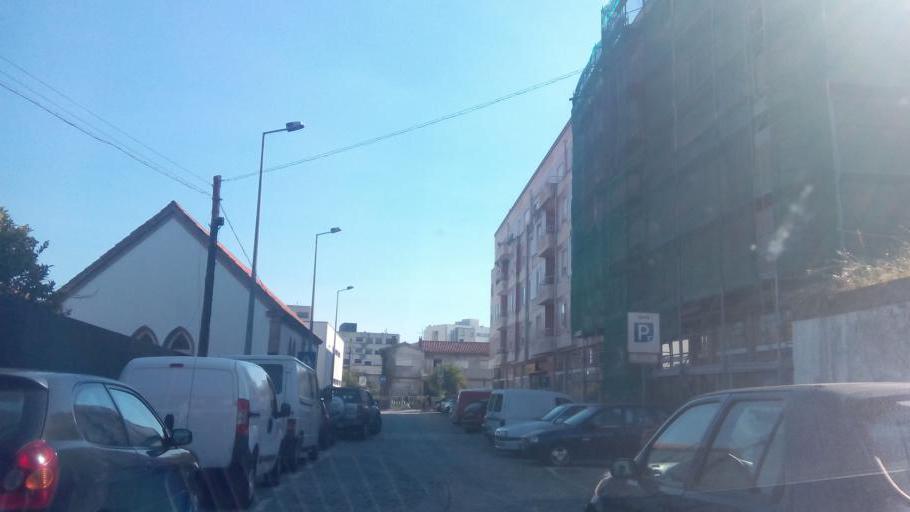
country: PT
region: Porto
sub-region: Paredes
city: Paredes
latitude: 41.2083
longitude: -8.3349
